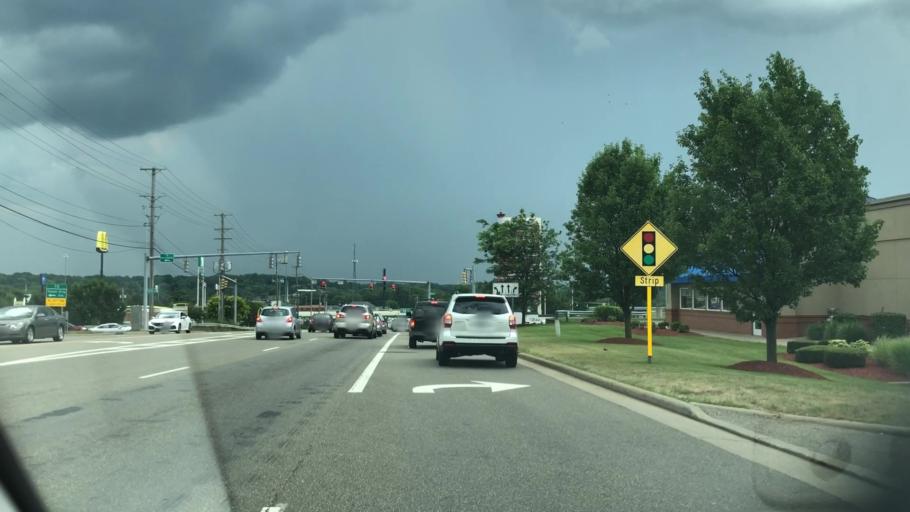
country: US
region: Ohio
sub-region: Stark County
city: North Canton
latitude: 40.8796
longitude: -81.4367
